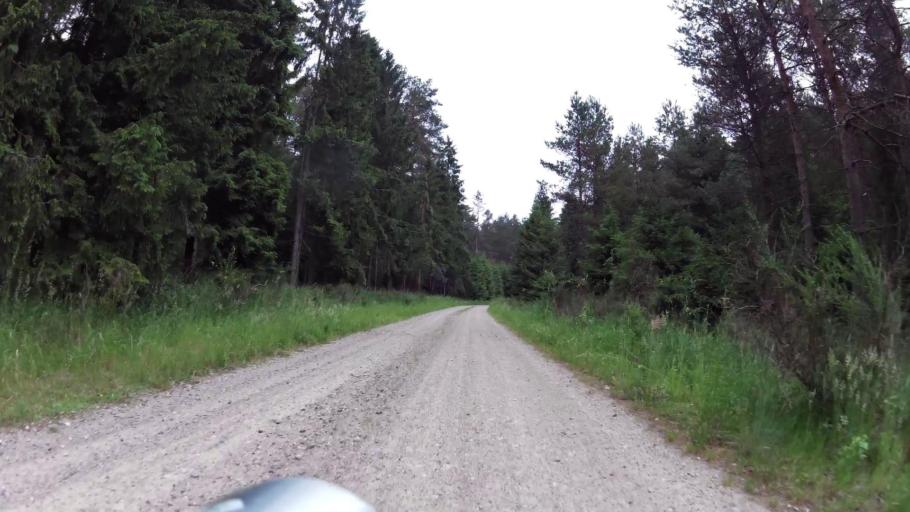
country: PL
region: West Pomeranian Voivodeship
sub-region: Powiat szczecinecki
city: Bialy Bor
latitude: 53.9495
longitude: 16.8290
